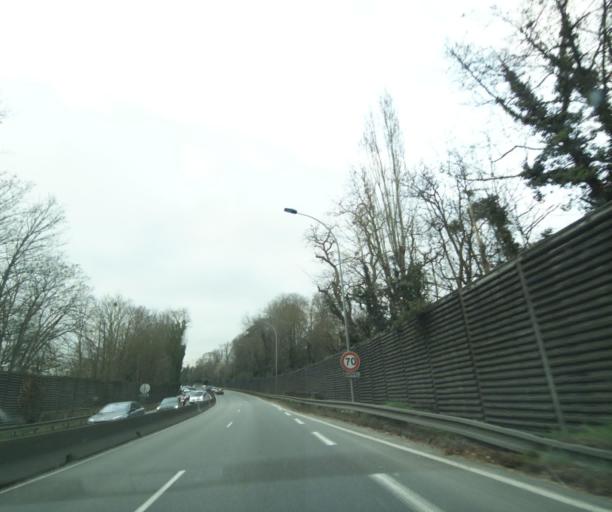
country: FR
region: Ile-de-France
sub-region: Departement des Yvelines
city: Saint-Germain-en-Laye
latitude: 48.8951
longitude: 2.0813
